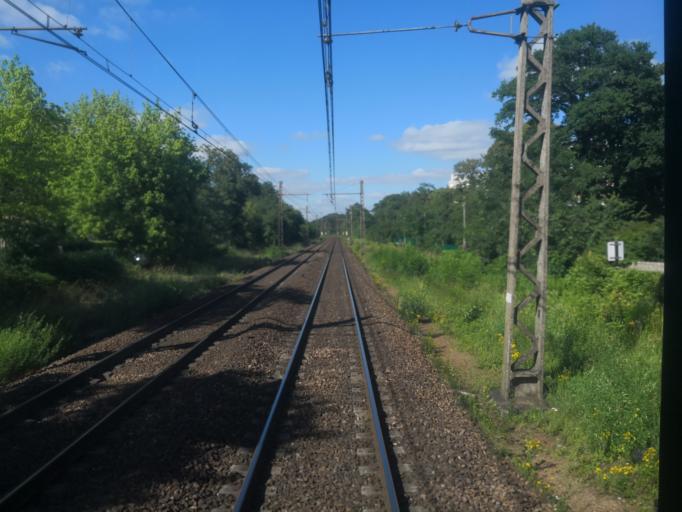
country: FR
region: Ile-de-France
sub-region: Departement de Seine-et-Marne
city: Avon
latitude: 48.4209
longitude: 2.7301
